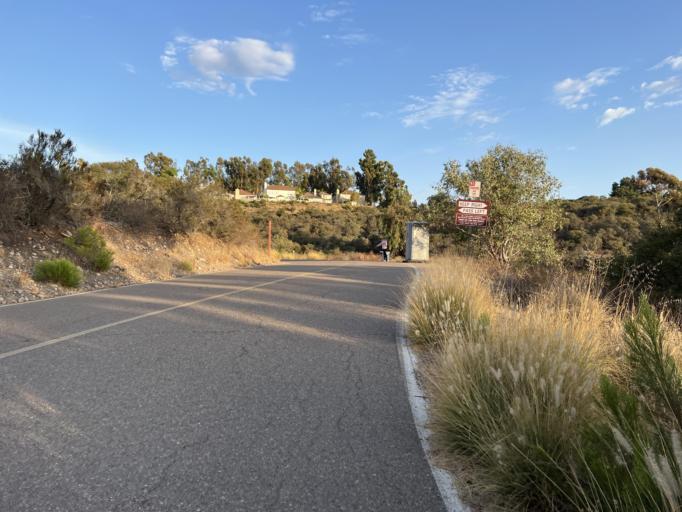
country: US
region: California
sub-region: San Diego County
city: Poway
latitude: 32.9206
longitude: -117.0891
